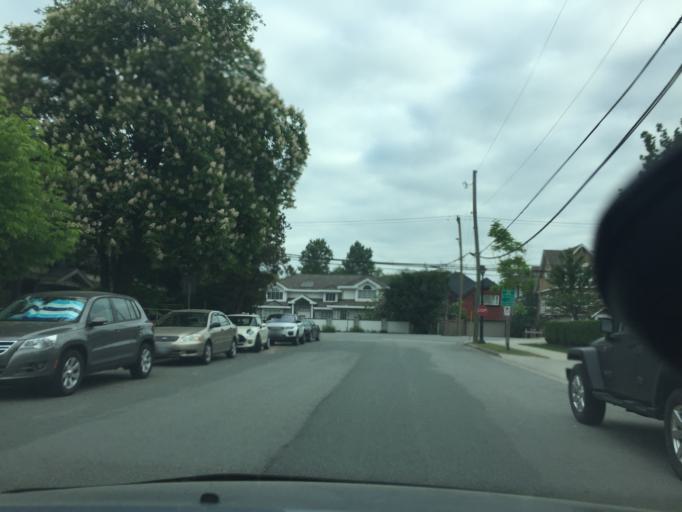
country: CA
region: British Columbia
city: Richmond
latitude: 49.1623
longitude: -123.1198
